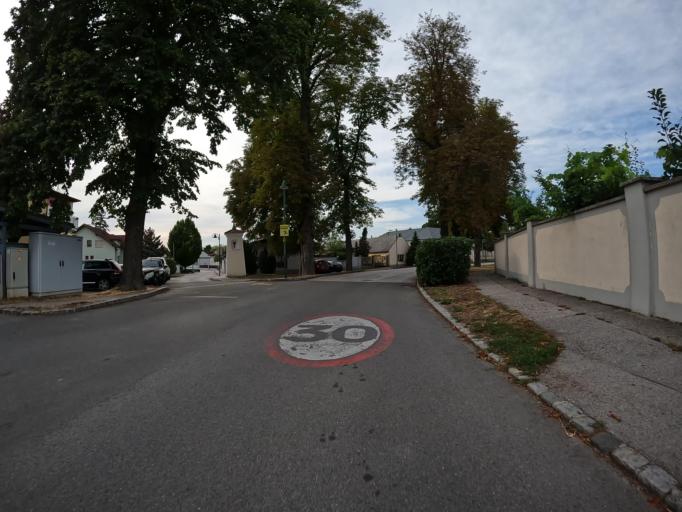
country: AT
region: Lower Austria
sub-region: Politischer Bezirk Baden
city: Trumau
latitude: 47.9951
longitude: 16.3408
